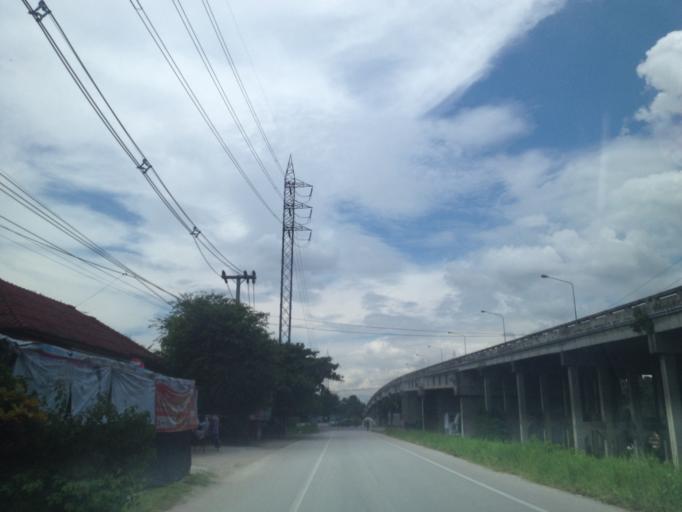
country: TH
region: Chiang Mai
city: Saraphi
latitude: 18.7200
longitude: 98.9848
